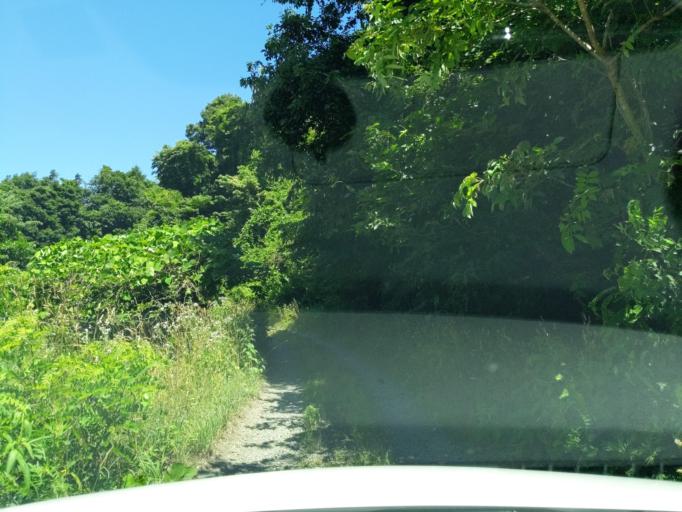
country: JP
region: Fukushima
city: Koriyama
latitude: 37.3871
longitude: 140.2519
